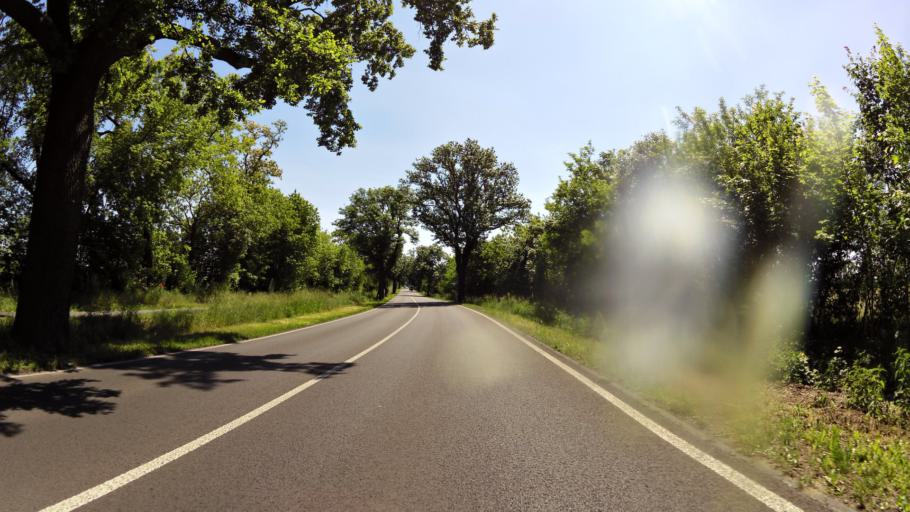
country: DE
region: Brandenburg
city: Lebus
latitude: 52.3873
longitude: 14.5177
